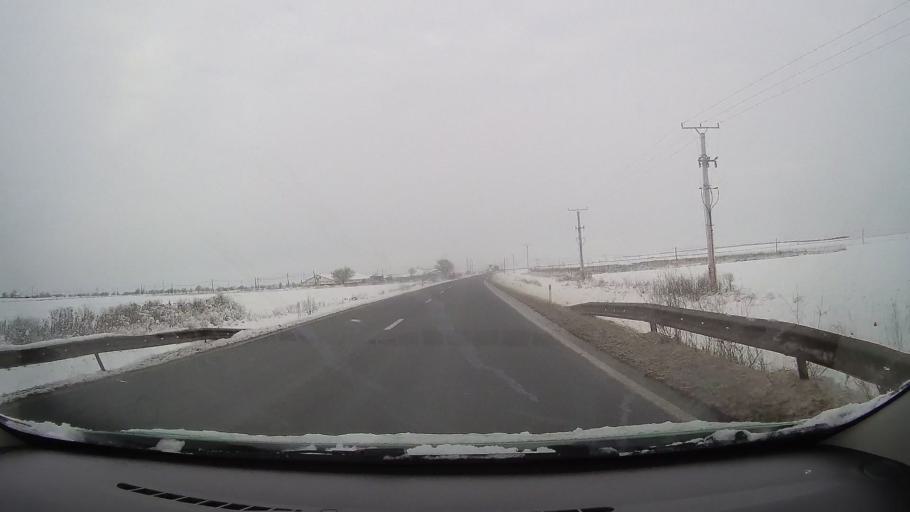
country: RO
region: Alba
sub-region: Municipiul Sebes
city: Lancram
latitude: 45.9679
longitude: 23.5290
